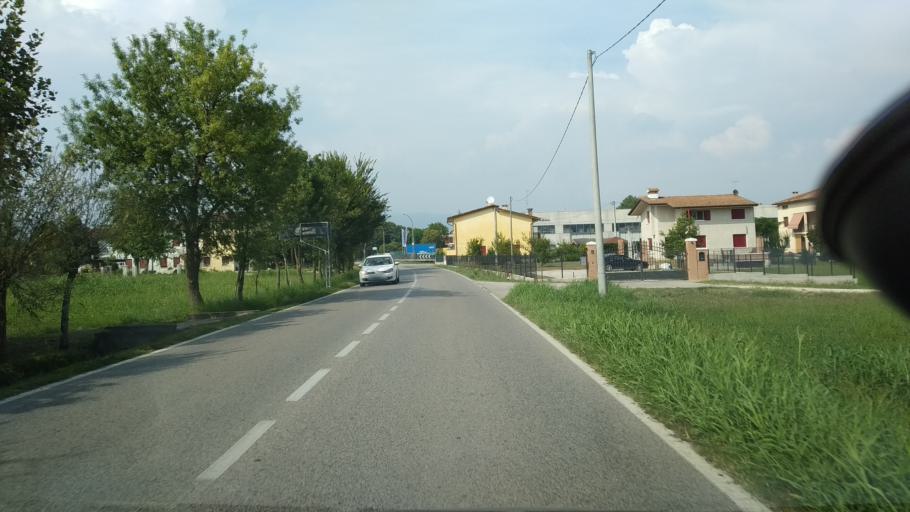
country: IT
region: Veneto
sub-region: Provincia di Vicenza
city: Pozzoleone
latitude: 45.6694
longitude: 11.6832
